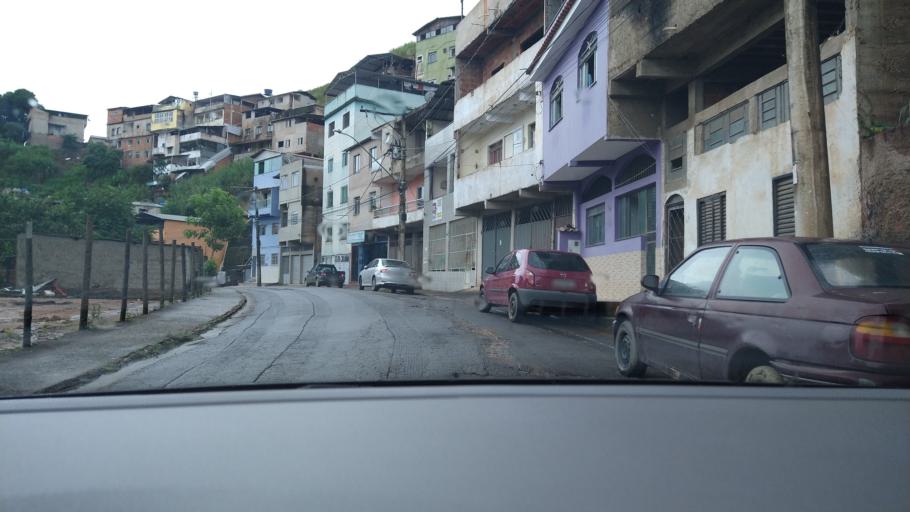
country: BR
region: Minas Gerais
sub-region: Ponte Nova
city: Ponte Nova
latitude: -20.4021
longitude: -42.8983
